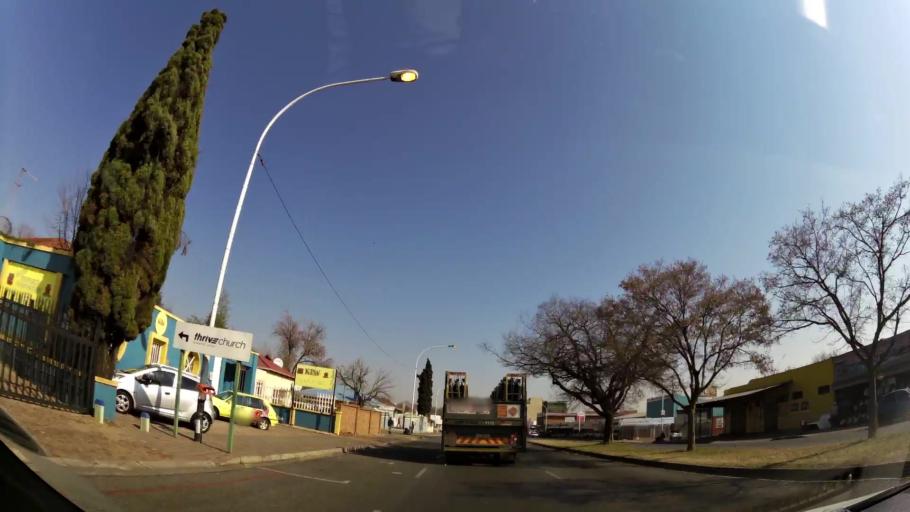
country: ZA
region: Gauteng
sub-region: Ekurhuleni Metropolitan Municipality
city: Boksburg
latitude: -26.2245
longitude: 28.2616
